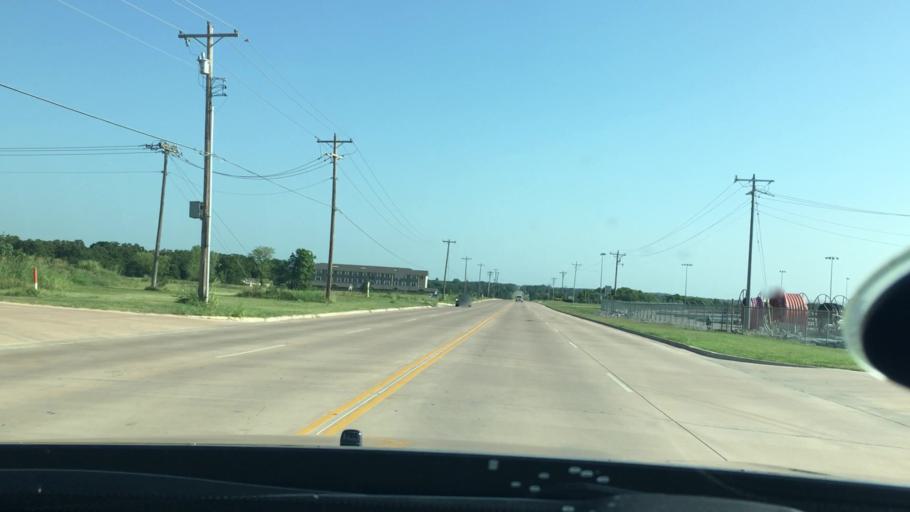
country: US
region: Oklahoma
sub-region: Pontotoc County
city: Ada
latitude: 34.7920
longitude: -96.6524
